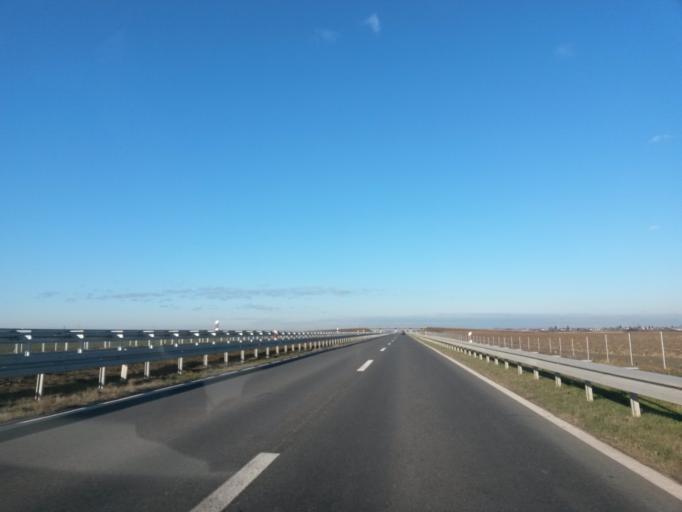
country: HR
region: Osjecko-Baranjska
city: Visnjevac
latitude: 45.5616
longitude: 18.5982
